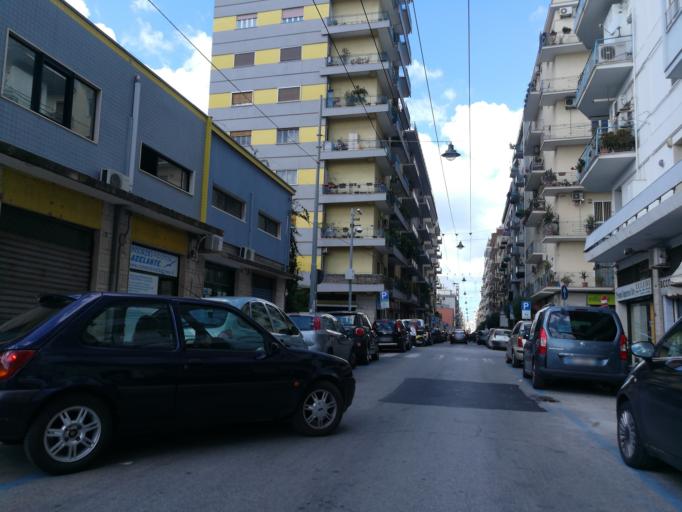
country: IT
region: Apulia
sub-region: Provincia di Bari
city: Bari
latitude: 41.1174
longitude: 16.8870
